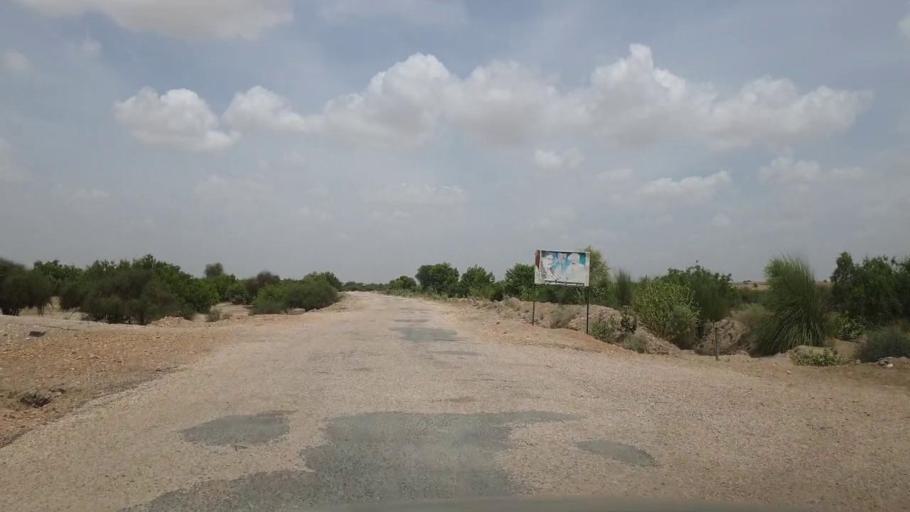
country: PK
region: Sindh
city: Kot Diji
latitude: 27.2026
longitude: 69.1308
